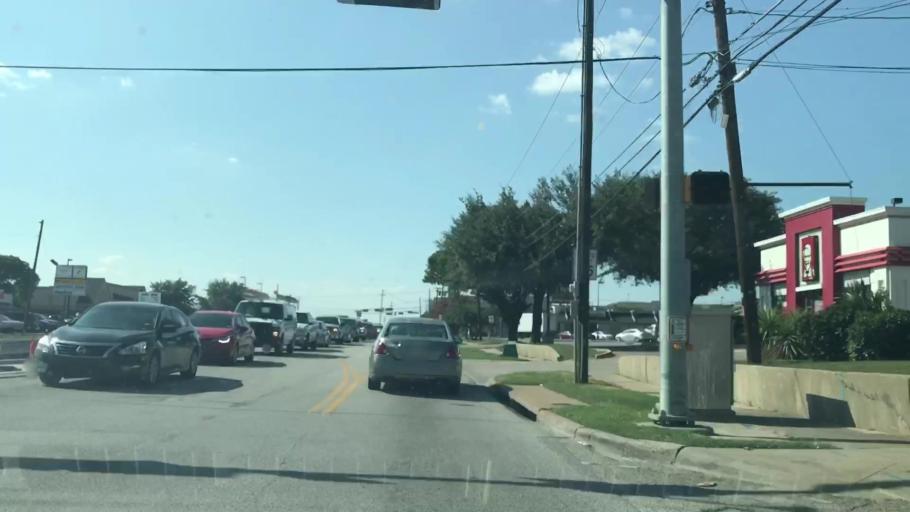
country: US
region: Texas
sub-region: Dallas County
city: Mesquite
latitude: 32.8223
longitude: -96.6446
